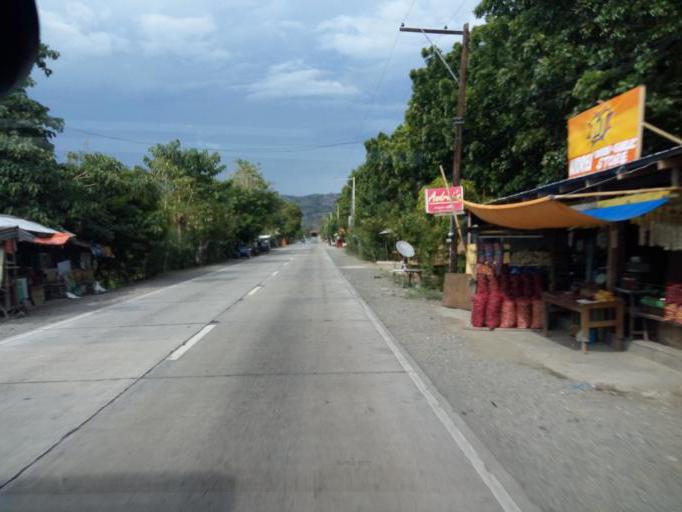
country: PH
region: Central Luzon
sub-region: Province of Nueva Ecija
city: Tayabo
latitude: 15.8256
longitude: 121.0176
